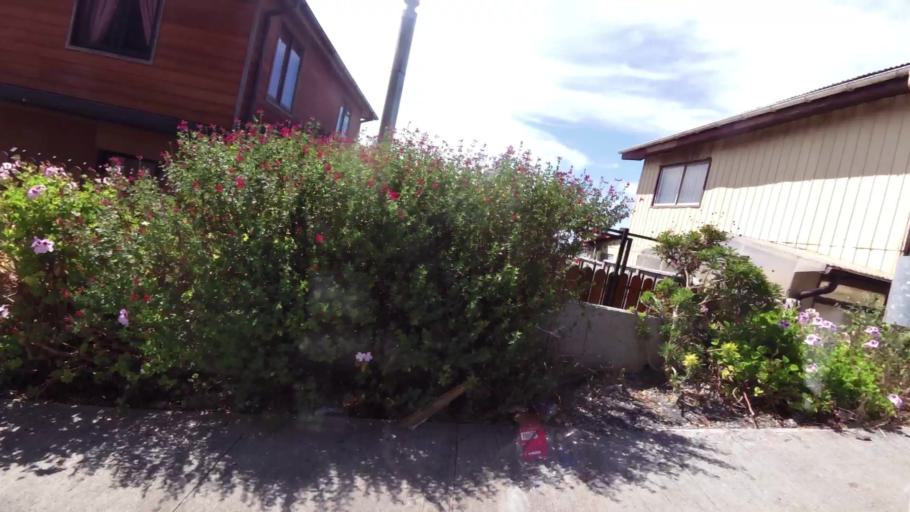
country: CL
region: Biobio
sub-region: Provincia de Concepcion
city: Talcahuano
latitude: -36.7081
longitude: -73.1185
